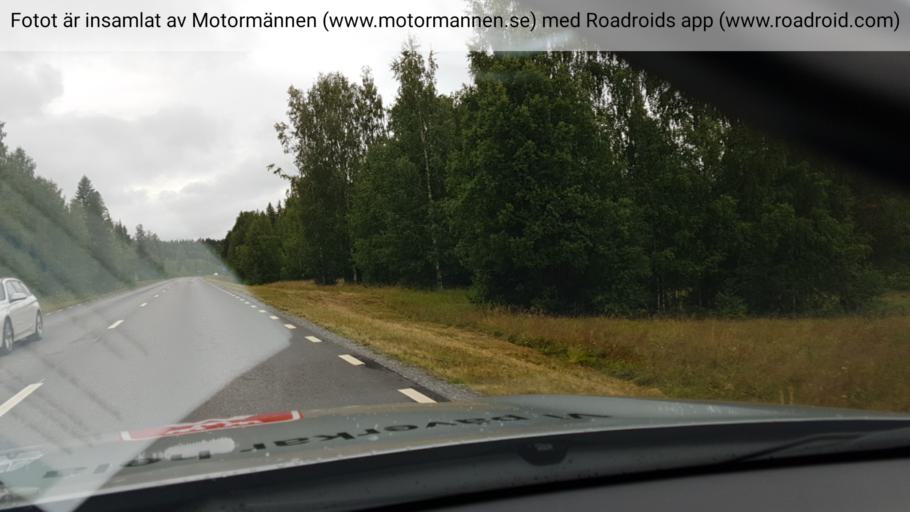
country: SE
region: Norrbotten
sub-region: Alvsbyns Kommun
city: AElvsbyn
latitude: 66.3354
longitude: 20.7562
